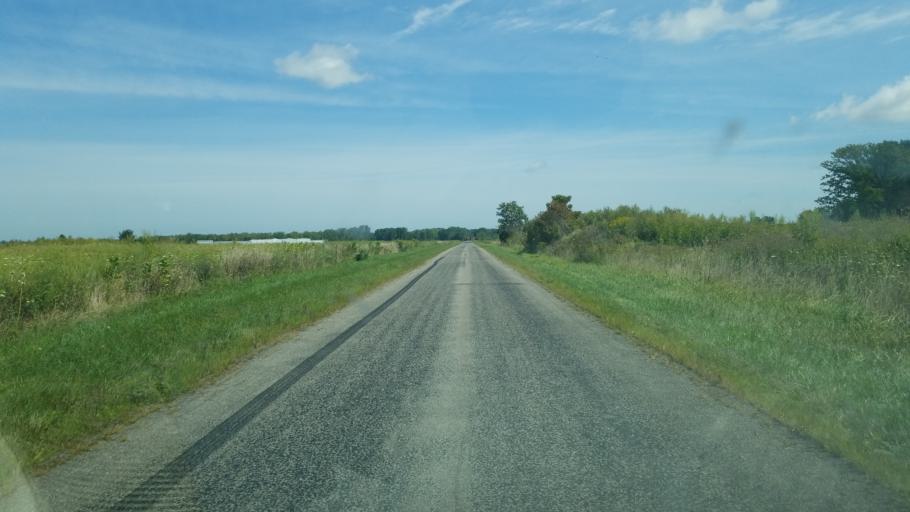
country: US
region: Ohio
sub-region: Hardin County
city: Kenton
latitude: 40.6097
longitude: -83.6434
